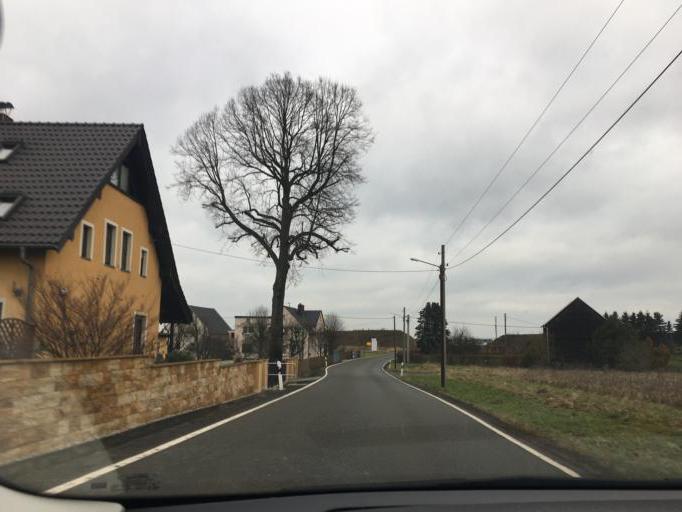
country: DE
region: Saxony
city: Hohenstein-Ernstthal
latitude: 50.8062
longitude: 12.7052
